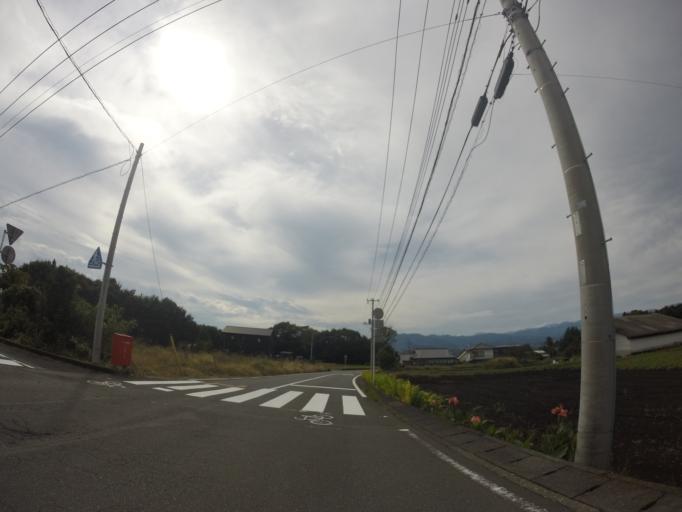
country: JP
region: Shizuoka
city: Fuji
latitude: 35.2179
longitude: 138.6836
